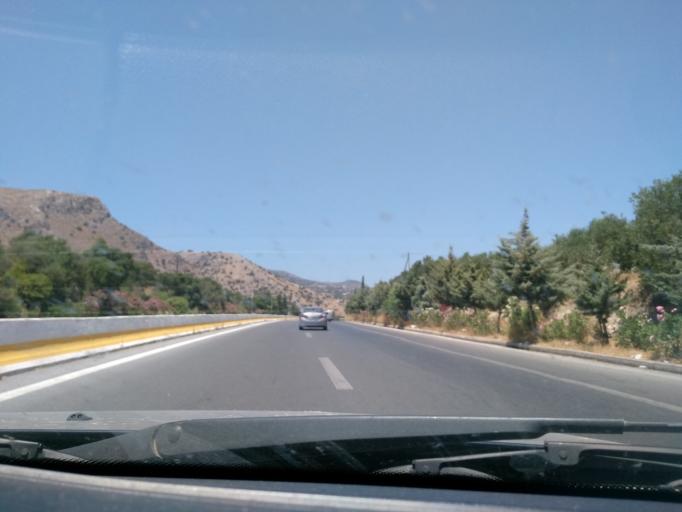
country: GR
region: Crete
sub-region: Nomos Irakleiou
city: Gazi
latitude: 35.3261
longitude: 25.0559
